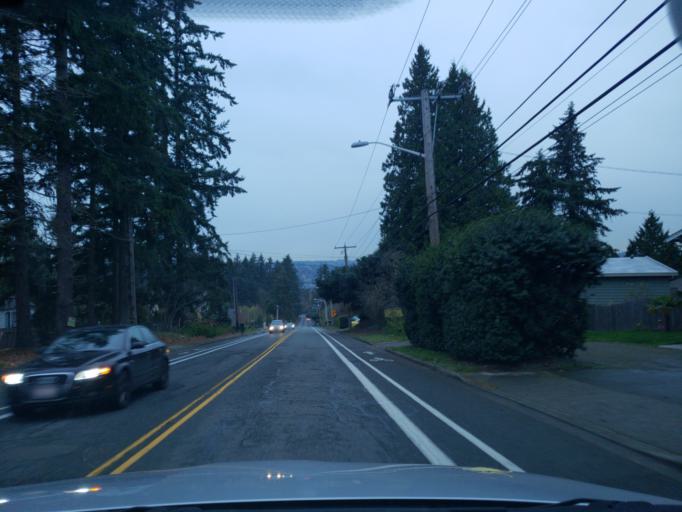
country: US
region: Washington
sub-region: King County
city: Kenmore
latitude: 47.7461
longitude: -122.2297
